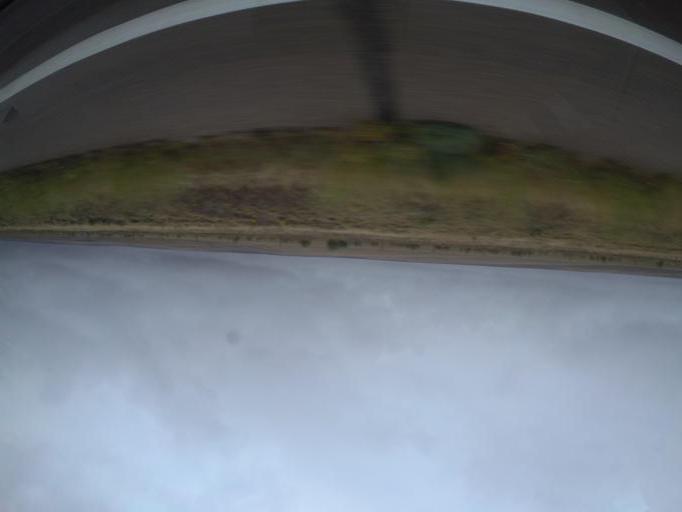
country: US
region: Colorado
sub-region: Arapahoe County
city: Byers
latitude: 39.7400
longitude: -103.7765
